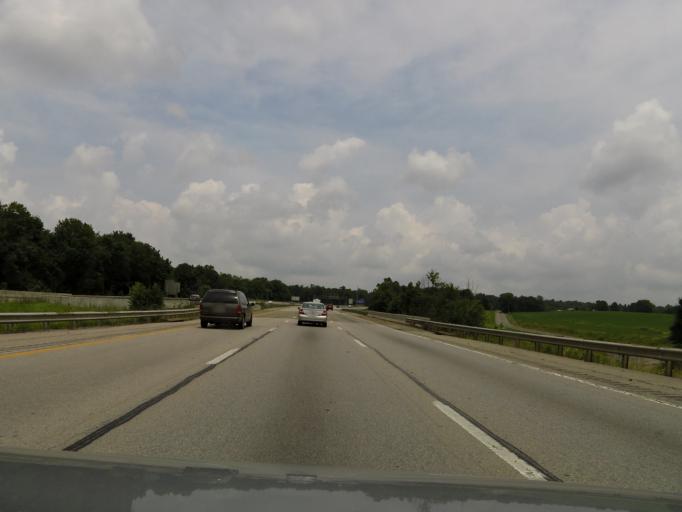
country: US
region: Kentucky
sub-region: Hardin County
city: Elizabethtown
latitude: 37.6865
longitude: -85.8424
